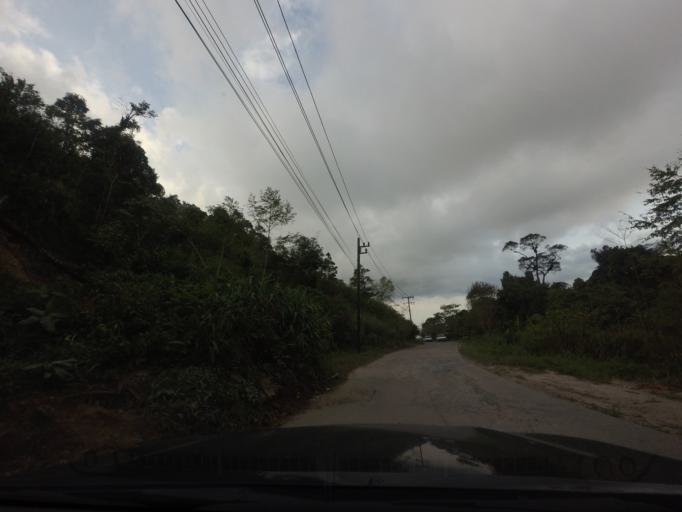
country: TH
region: Phetchabun
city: Lom Kao
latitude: 16.8957
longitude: 101.1044
